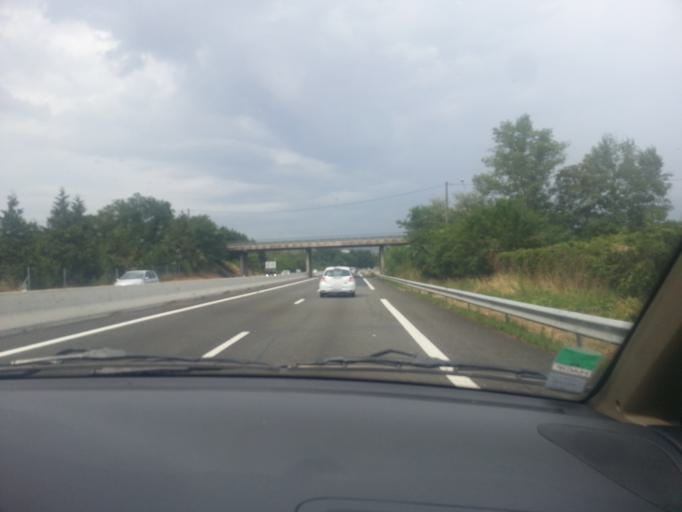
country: FR
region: Auvergne
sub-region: Departement du Puy-de-Dome
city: Issoire
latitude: 45.5328
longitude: 3.2576
